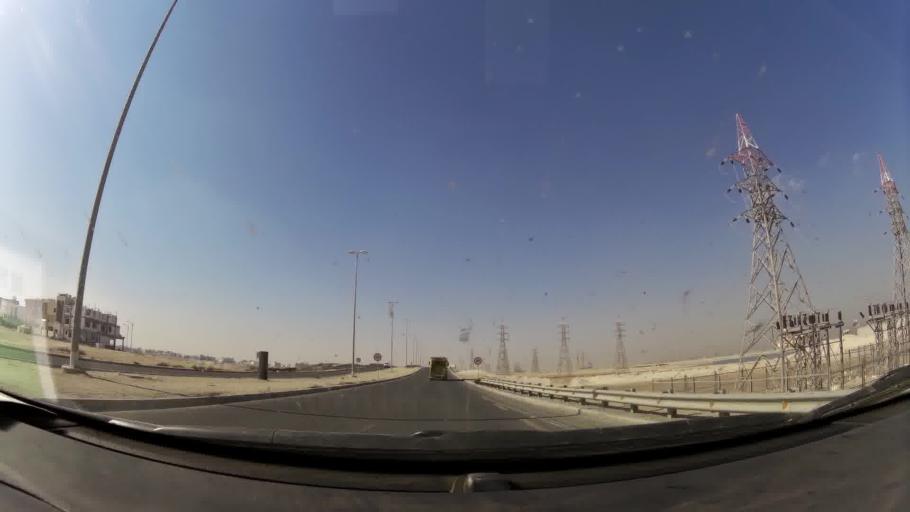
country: SA
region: Eastern Province
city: Al Khafji
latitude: 28.6751
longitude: 48.3581
